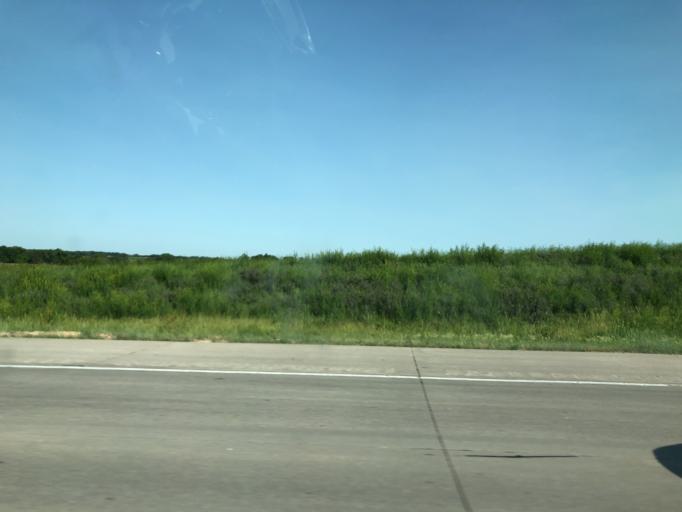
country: US
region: Nebraska
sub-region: Saunders County
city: Ashland
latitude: 40.9803
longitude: -96.3760
